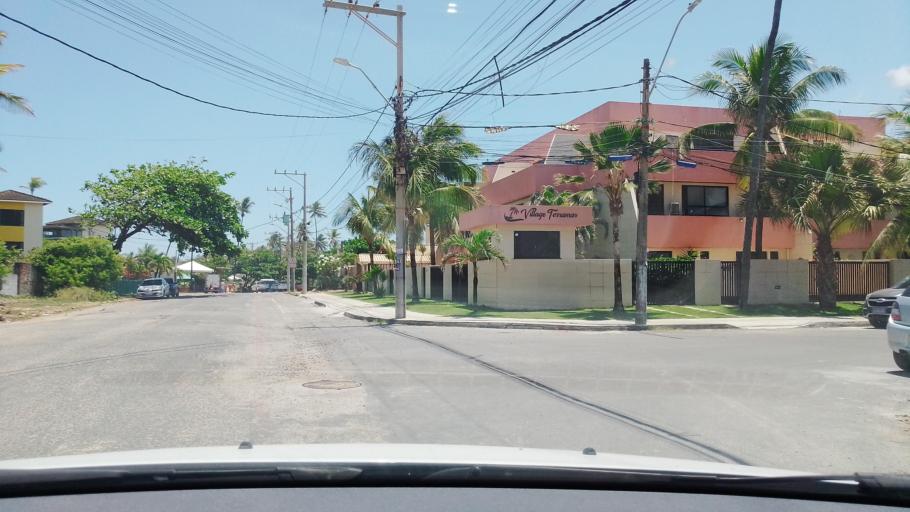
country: BR
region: Bahia
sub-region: Lauro De Freitas
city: Lauro de Freitas
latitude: -12.9339
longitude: -38.3254
